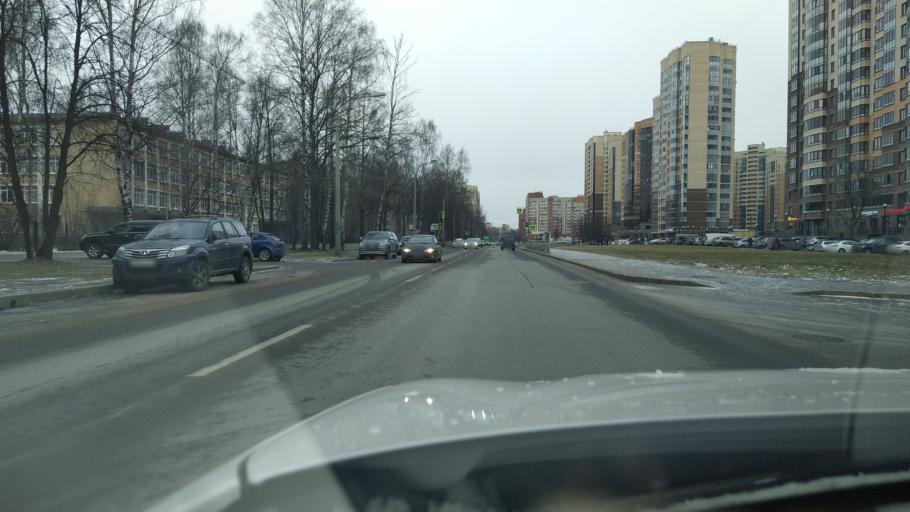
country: RU
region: Leningrad
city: Kalininskiy
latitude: 60.0028
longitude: 30.3976
